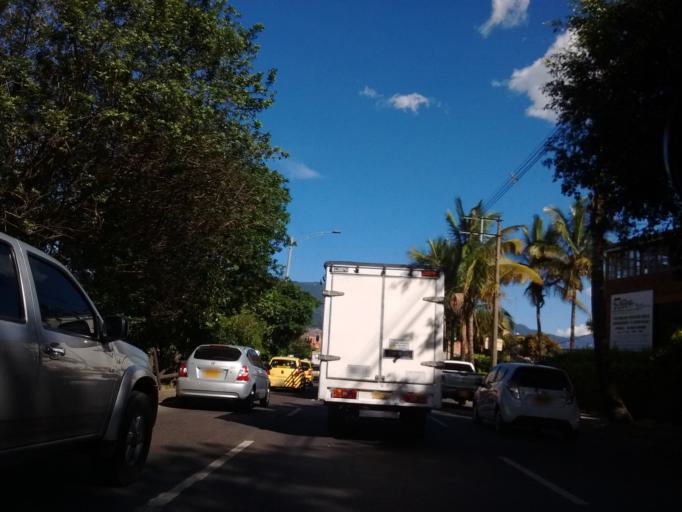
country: CO
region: Antioquia
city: Medellin
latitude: 6.2618
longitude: -75.5853
